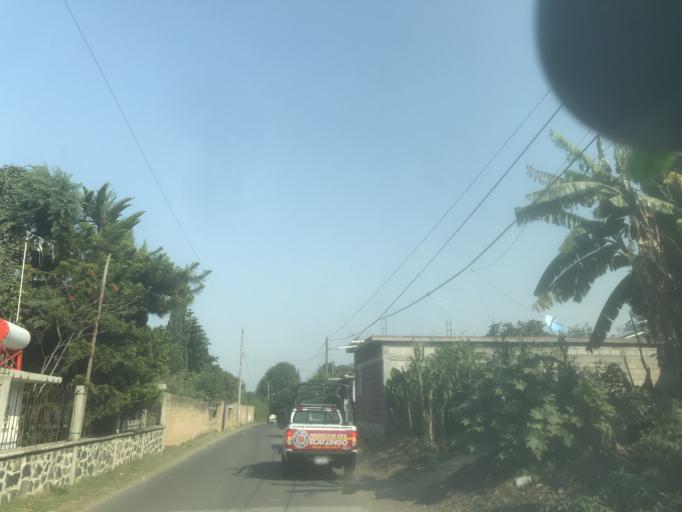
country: MX
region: Morelos
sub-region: Yecapixtla
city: Texcala
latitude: 18.9325
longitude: -98.7975
